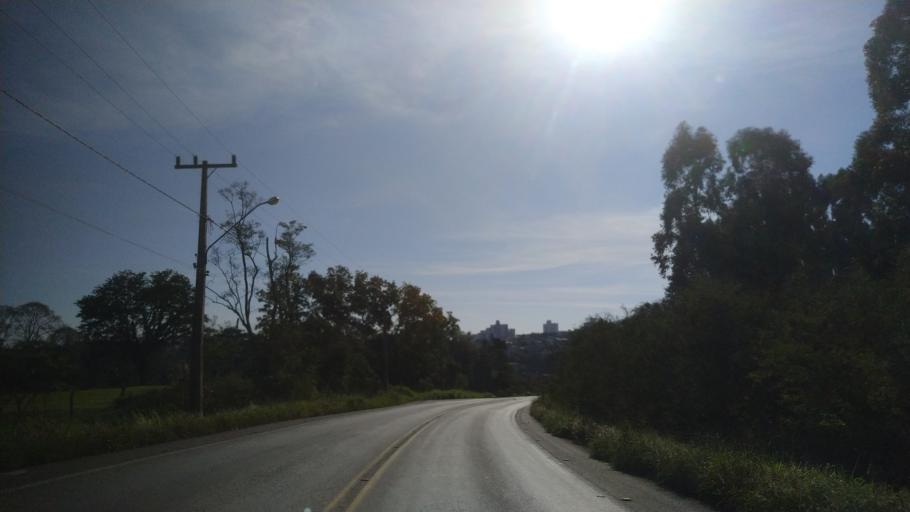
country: BR
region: Santa Catarina
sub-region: Chapeco
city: Chapeco
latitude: -27.1155
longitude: -52.6311
